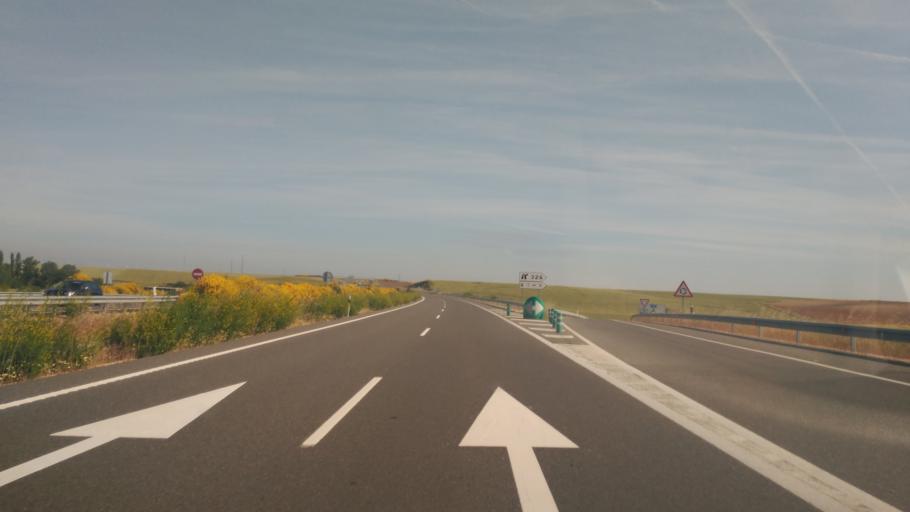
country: ES
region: Castille and Leon
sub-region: Provincia de Salamanca
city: Calzada de Valdunciel
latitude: 41.0845
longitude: -5.6889
